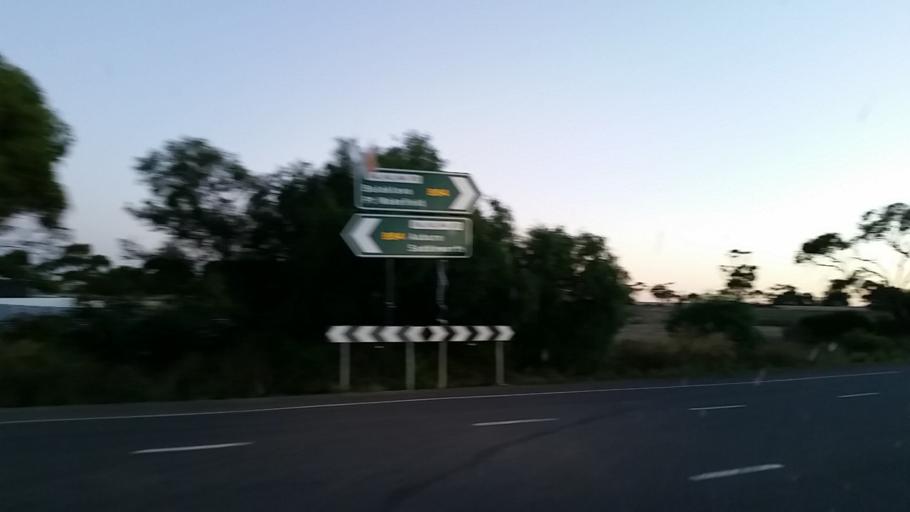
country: AU
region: South Australia
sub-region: Wakefield
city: Balaklava
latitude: -34.0938
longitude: 138.4992
